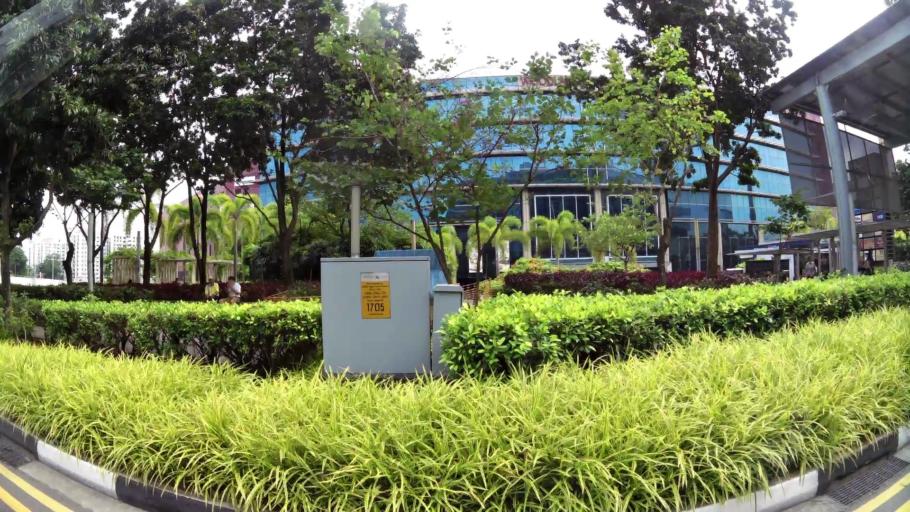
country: MY
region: Johor
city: Johor Bahru
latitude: 1.4357
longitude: 103.7866
